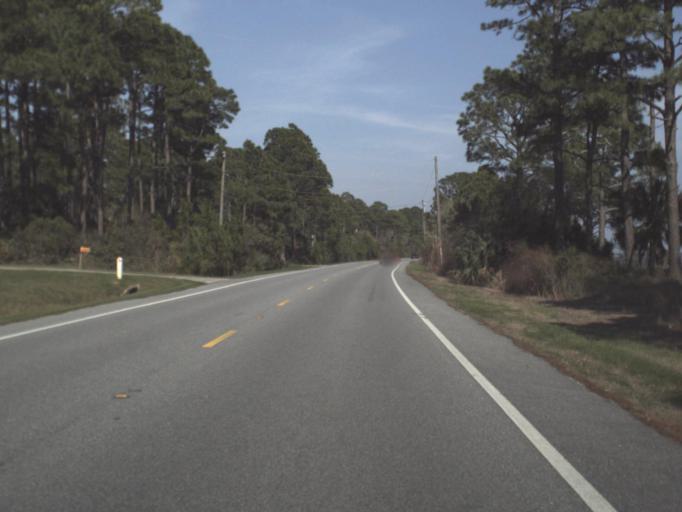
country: US
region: Florida
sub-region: Franklin County
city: Eastpoint
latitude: 29.7664
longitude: -84.8083
